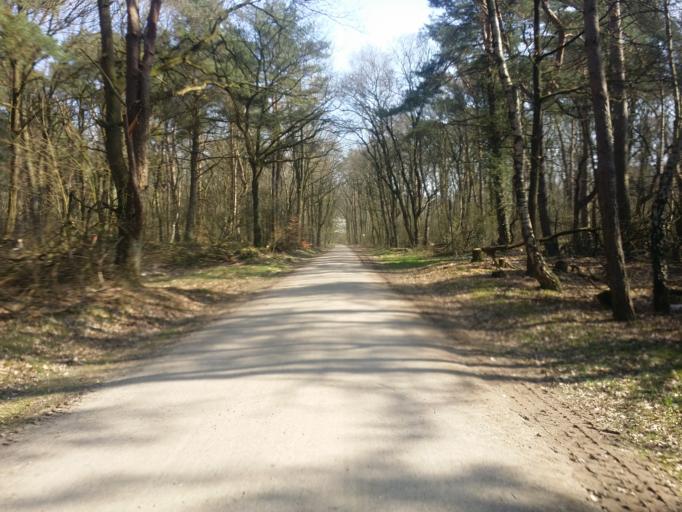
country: DE
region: Lower Saxony
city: Kirchseelte
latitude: 53.0128
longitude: 8.6809
